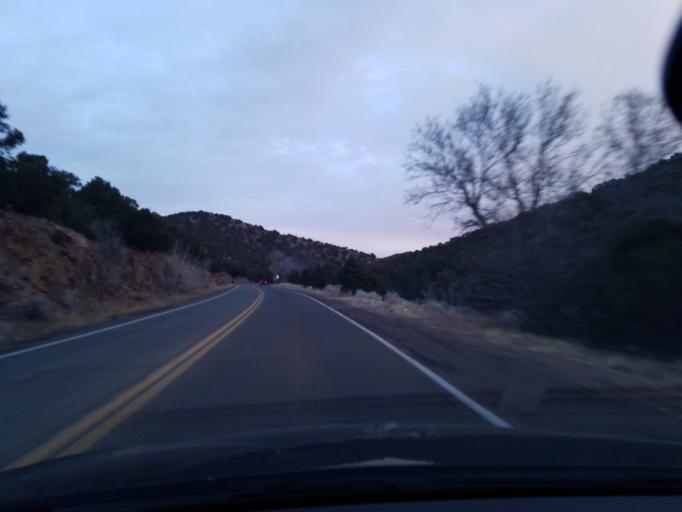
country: US
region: New Mexico
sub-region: Santa Fe County
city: Santa Fe
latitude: 35.7024
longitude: -105.9062
